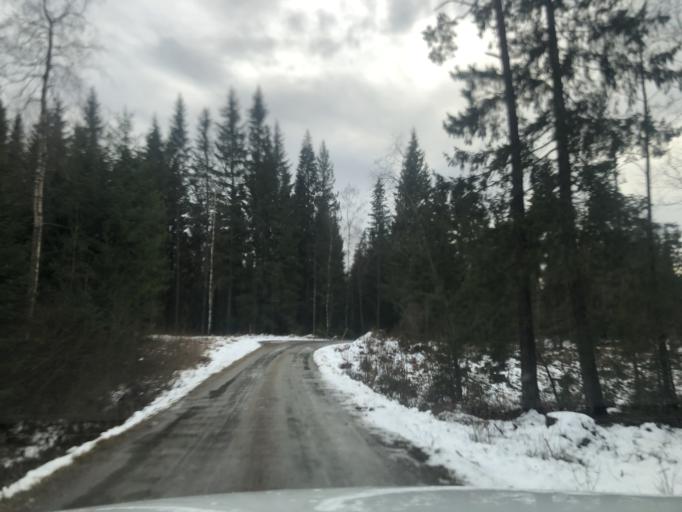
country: SE
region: Vaestra Goetaland
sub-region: Ulricehamns Kommun
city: Ulricehamn
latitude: 57.7741
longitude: 13.4734
